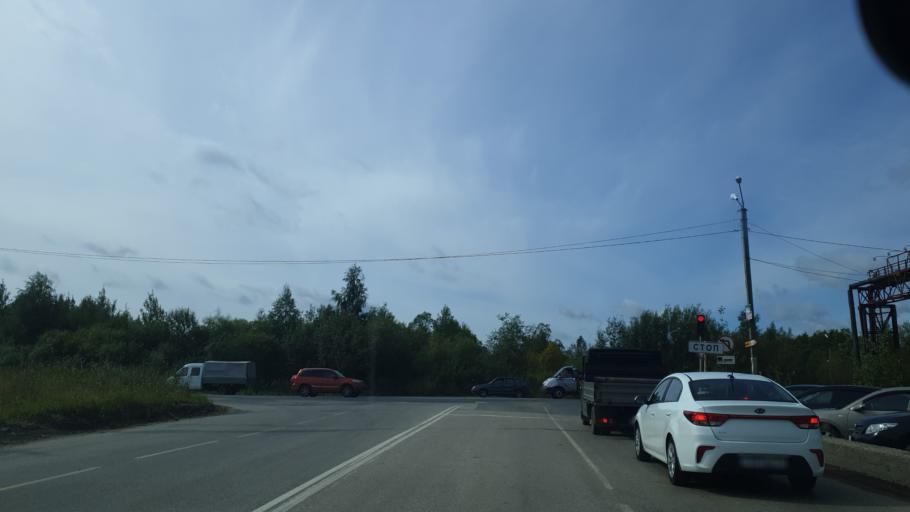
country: RU
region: Komi Republic
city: Ezhva
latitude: 61.8075
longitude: 50.7277
